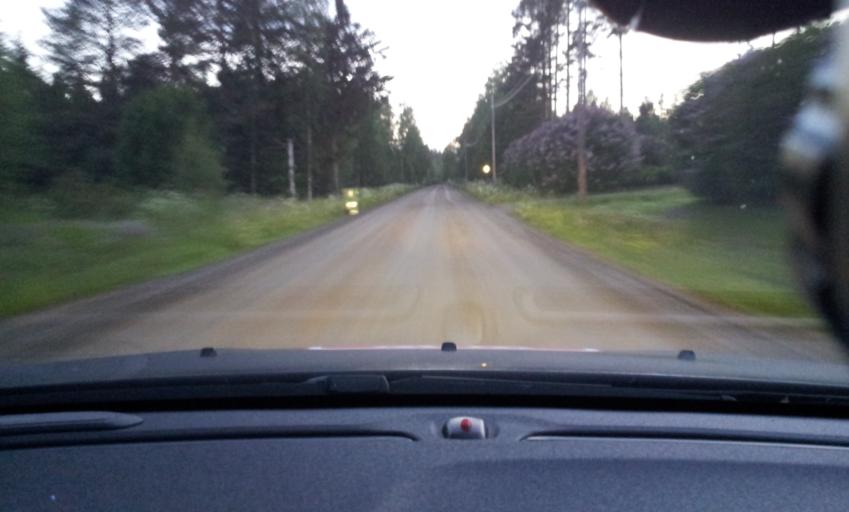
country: SE
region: Vaesternorrland
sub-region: Ange Kommun
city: Ange
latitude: 62.7690
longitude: 15.7557
